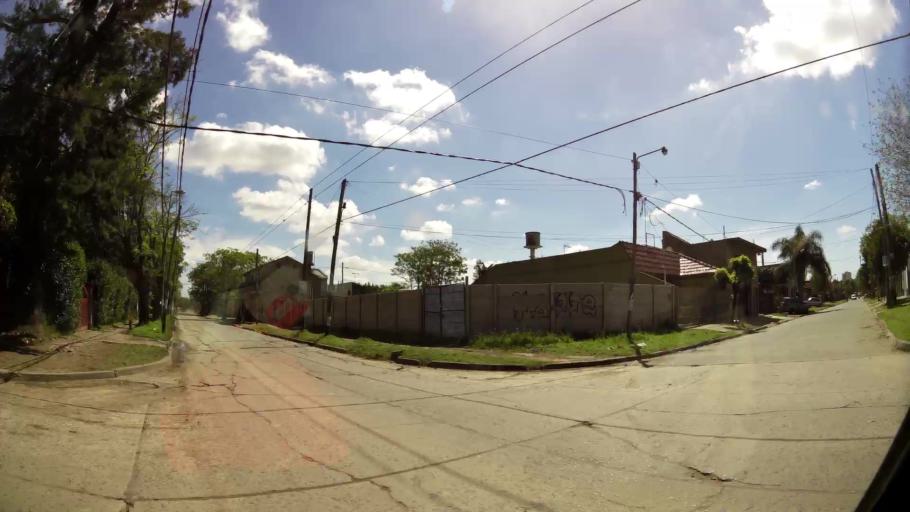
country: AR
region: Buenos Aires
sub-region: Partido de Quilmes
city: Quilmes
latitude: -34.8160
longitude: -58.2659
